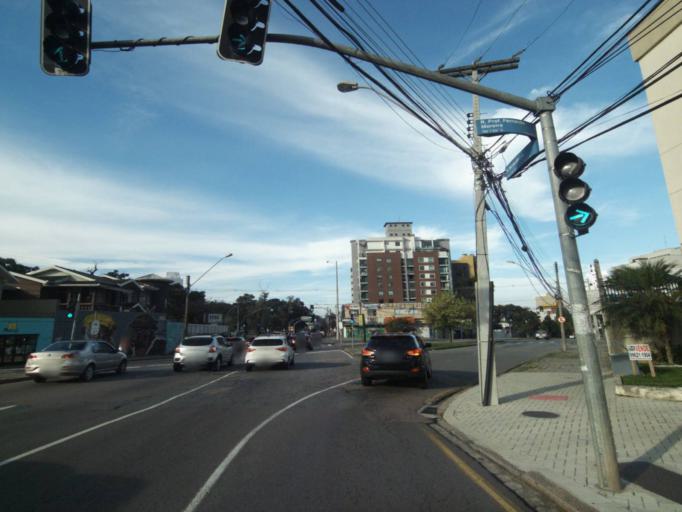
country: BR
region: Parana
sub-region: Curitiba
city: Curitiba
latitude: -25.4292
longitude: -49.2867
